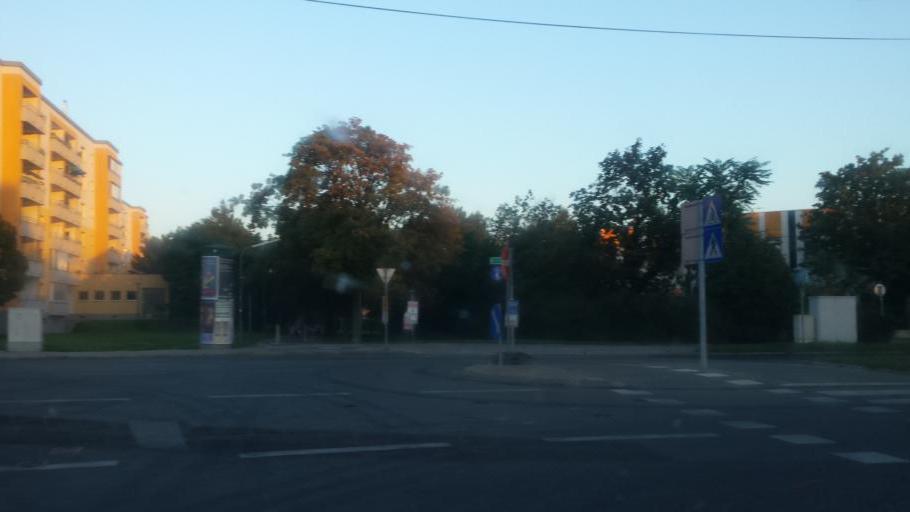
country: AT
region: Lower Austria
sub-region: Politischer Bezirk Wien-Umgebung
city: Schwechat
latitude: 48.1714
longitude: 16.4257
